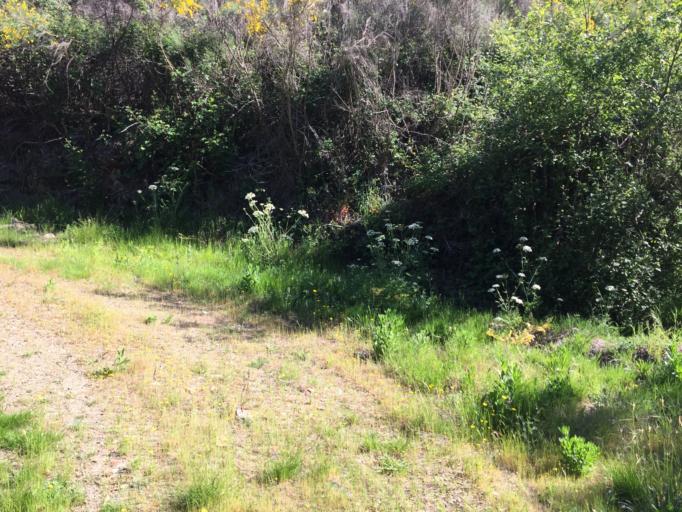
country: PT
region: Coimbra
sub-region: Pampilhosa da Serra
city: Pampilhosa da Serra
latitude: 40.0887
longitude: -7.7808
